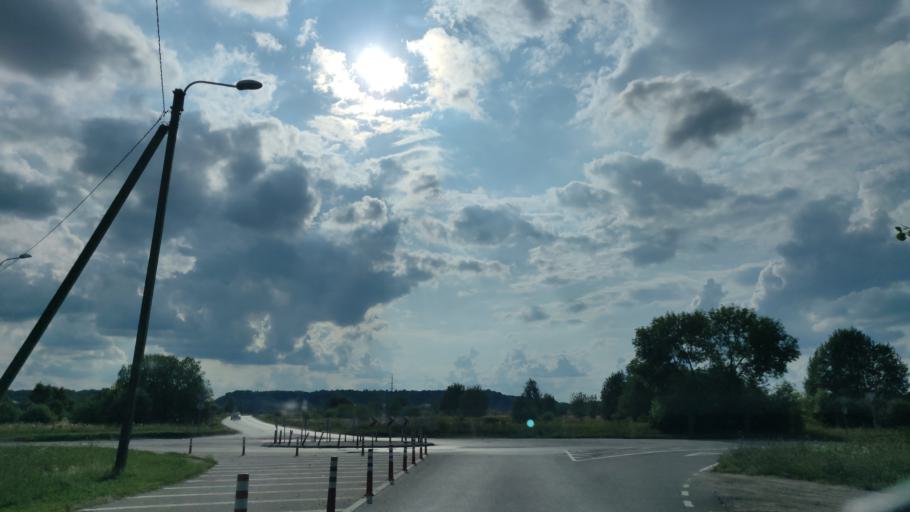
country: LT
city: Baltoji Voke
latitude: 54.6302
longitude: 25.1375
